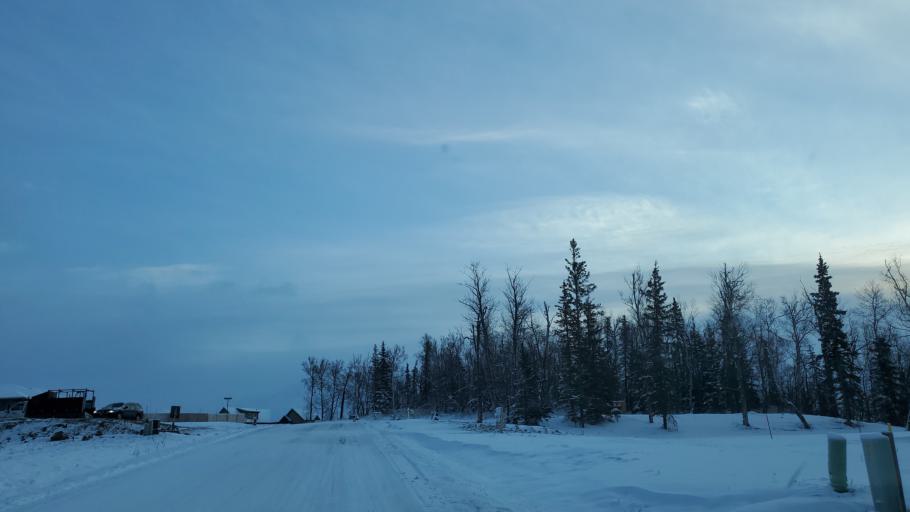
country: US
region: Alaska
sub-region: Matanuska-Susitna Borough
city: Lakes
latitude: 61.5455
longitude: -149.3260
